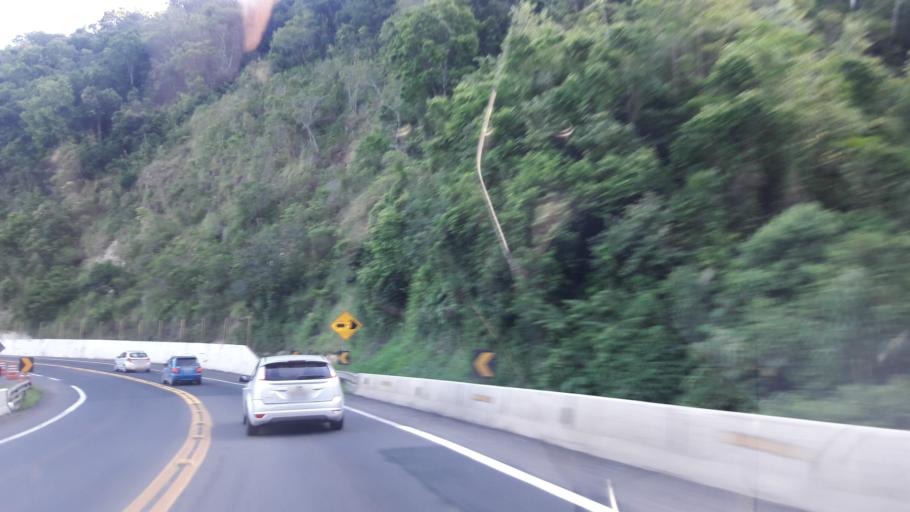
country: BR
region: Parana
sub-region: Prudentopolis
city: Prudentopolis
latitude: -25.3232
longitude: -51.1967
